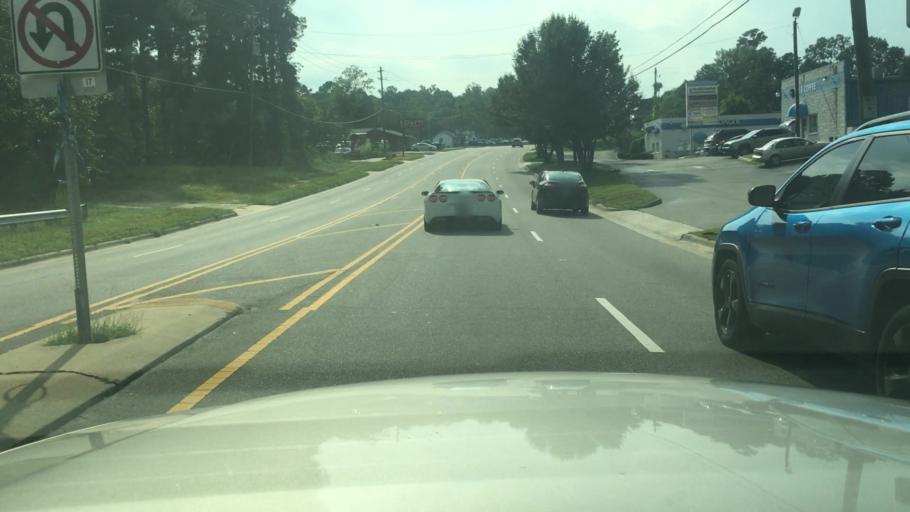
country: US
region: North Carolina
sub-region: Cumberland County
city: Fort Bragg
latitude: 35.0834
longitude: -78.9691
